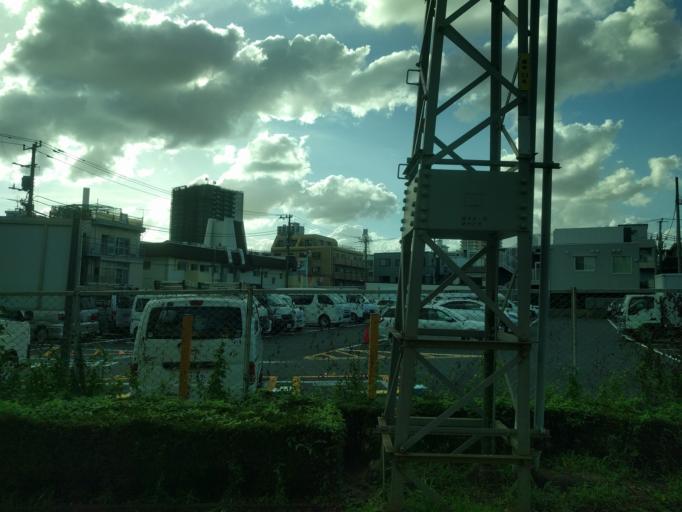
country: JP
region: Tokyo
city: Tokyo
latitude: 35.7364
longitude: 139.7274
